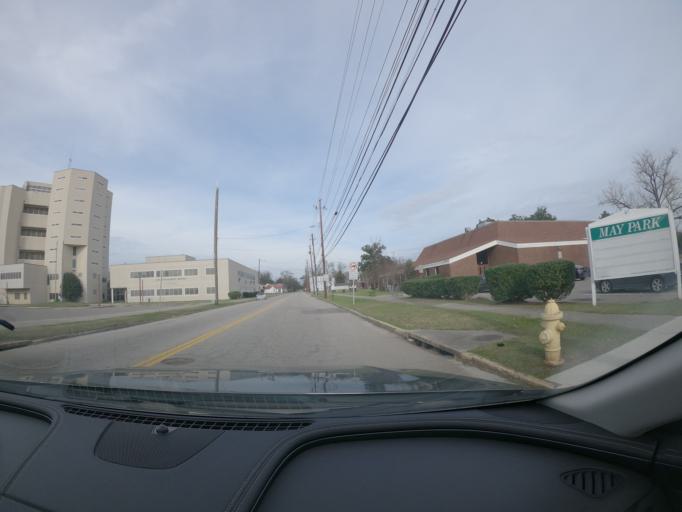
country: US
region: Georgia
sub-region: Richmond County
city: Augusta
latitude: 33.4652
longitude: -81.9597
